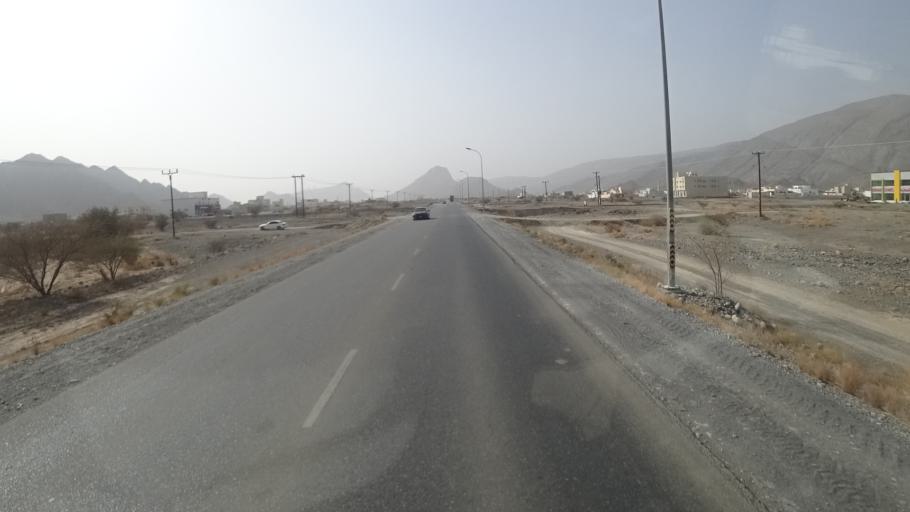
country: OM
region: Muhafazat ad Dakhiliyah
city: Nizwa
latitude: 23.0285
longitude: 57.4959
